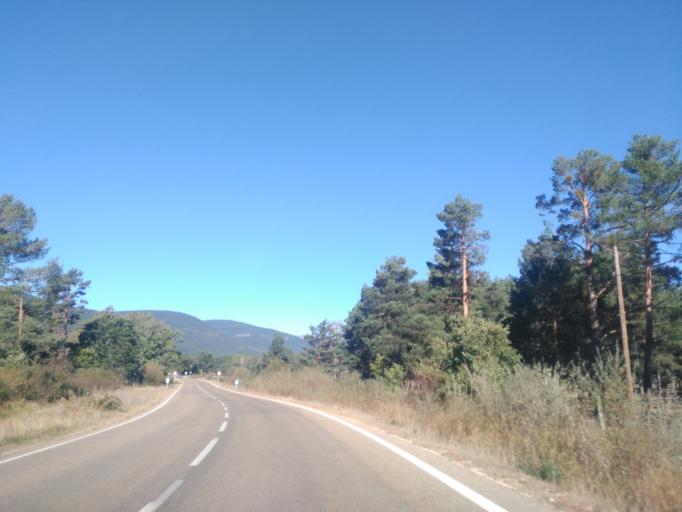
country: ES
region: Castille and Leon
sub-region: Provincia de Soria
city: Vinuesa
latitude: 41.9193
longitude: -2.7576
